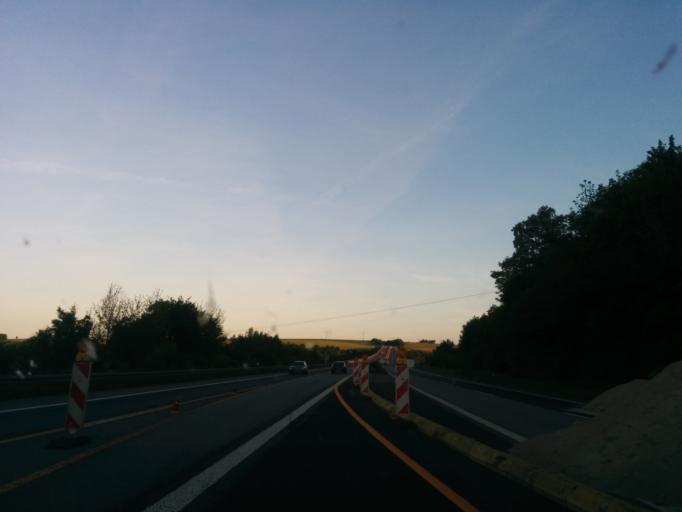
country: DE
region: Bavaria
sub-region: Regierungsbezirk Unterfranken
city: Segnitz
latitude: 49.6751
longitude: 10.1258
